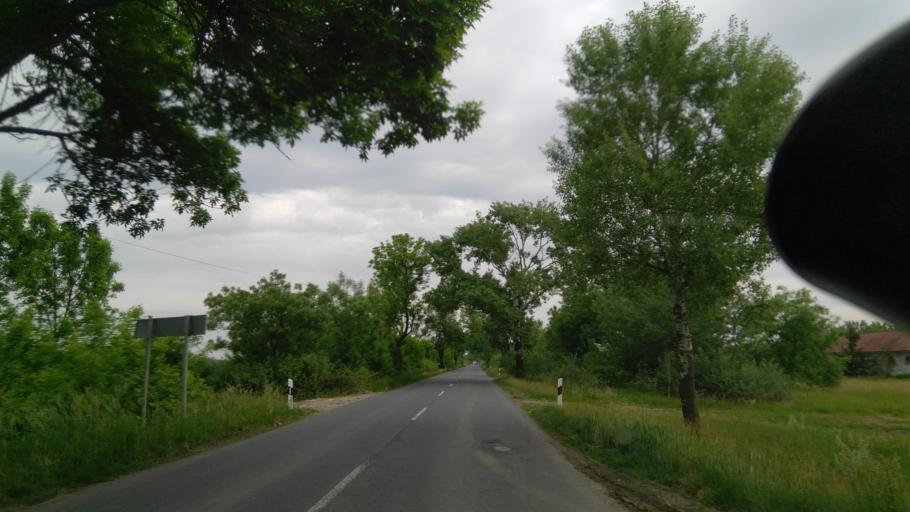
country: HU
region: Bekes
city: Veszto
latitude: 46.8948
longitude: 21.2474
